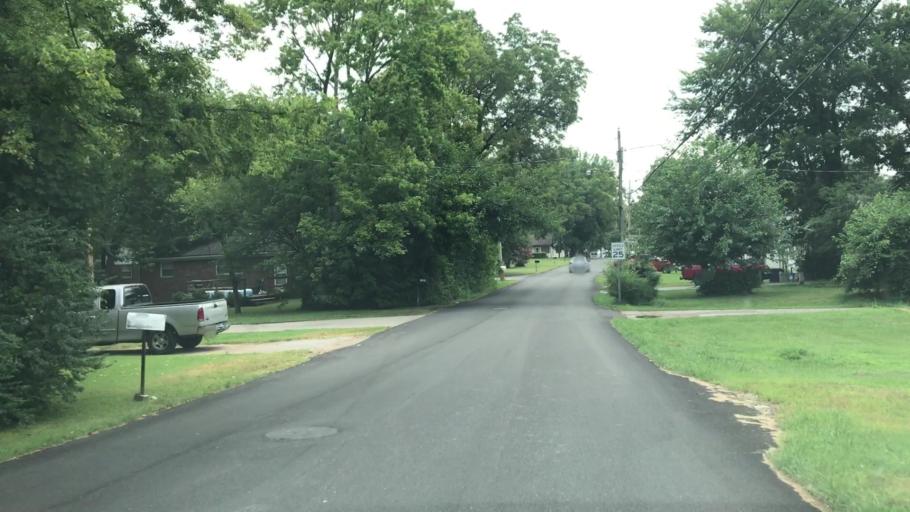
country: US
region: Kentucky
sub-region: Warren County
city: Bowling Green
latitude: 36.9760
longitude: -86.4409
